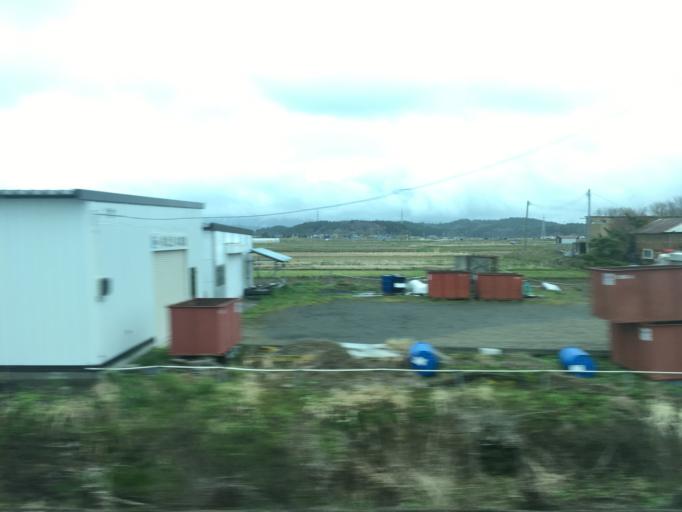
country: JP
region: Akita
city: Akita Shi
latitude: 39.7921
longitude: 140.0641
